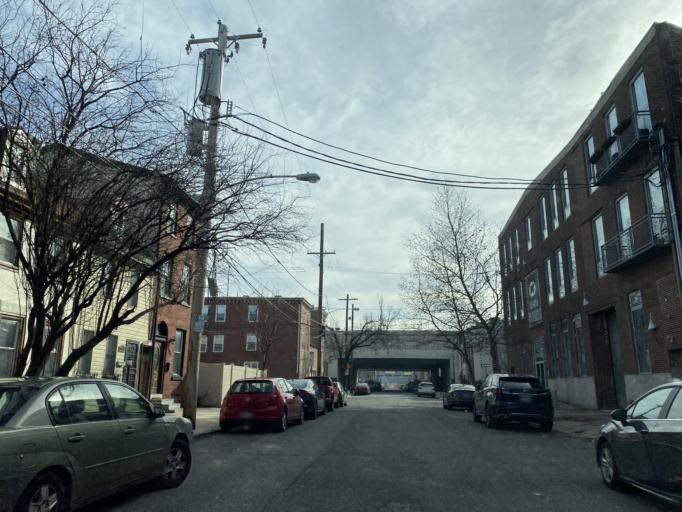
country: US
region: Pennsylvania
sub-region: Philadelphia County
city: Philadelphia
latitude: 39.9683
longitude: -75.1332
